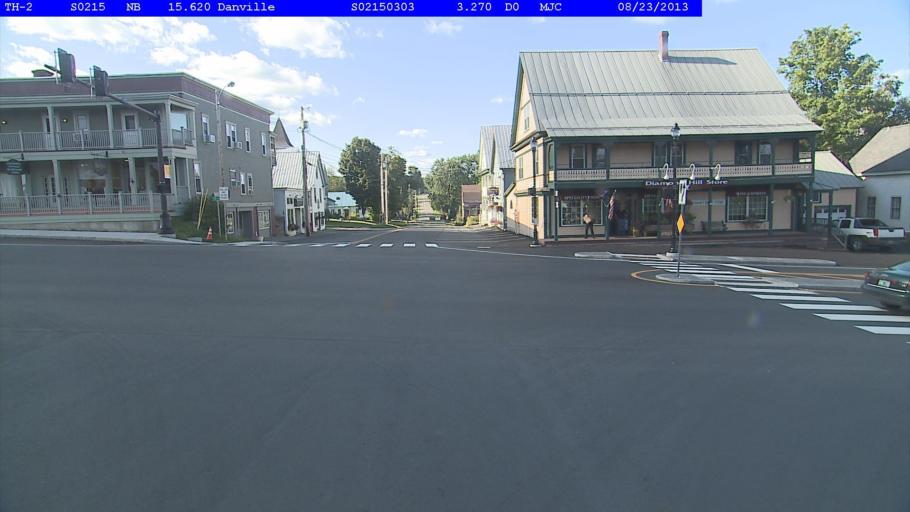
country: US
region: Vermont
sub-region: Caledonia County
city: Saint Johnsbury
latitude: 44.4113
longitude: -72.1400
